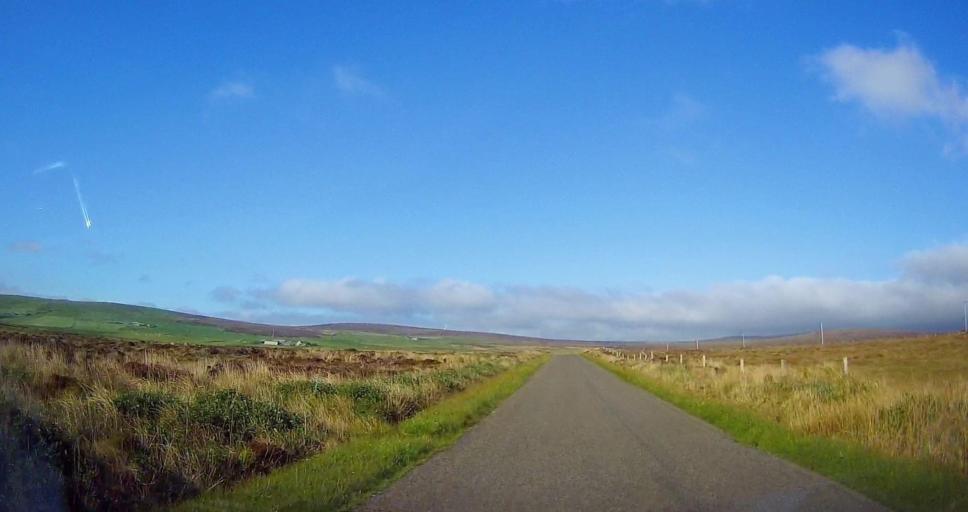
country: GB
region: Scotland
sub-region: Orkney Islands
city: Stromness
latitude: 59.0809
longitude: -3.1946
